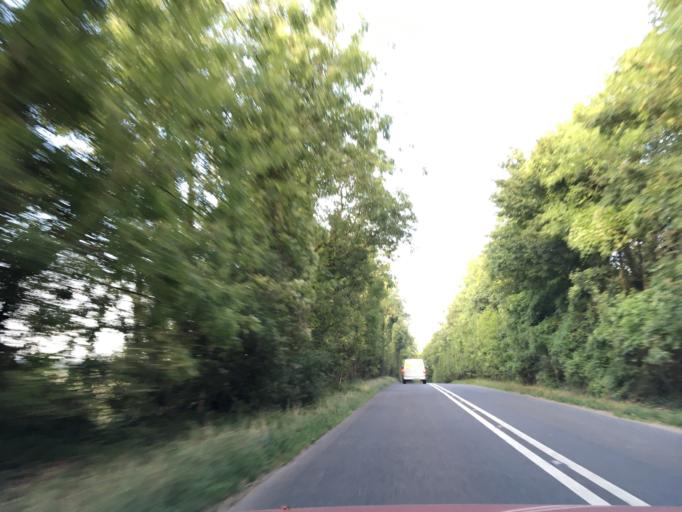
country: GB
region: England
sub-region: Gloucestershire
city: Bourton on the Water
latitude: 51.8786
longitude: -1.7802
